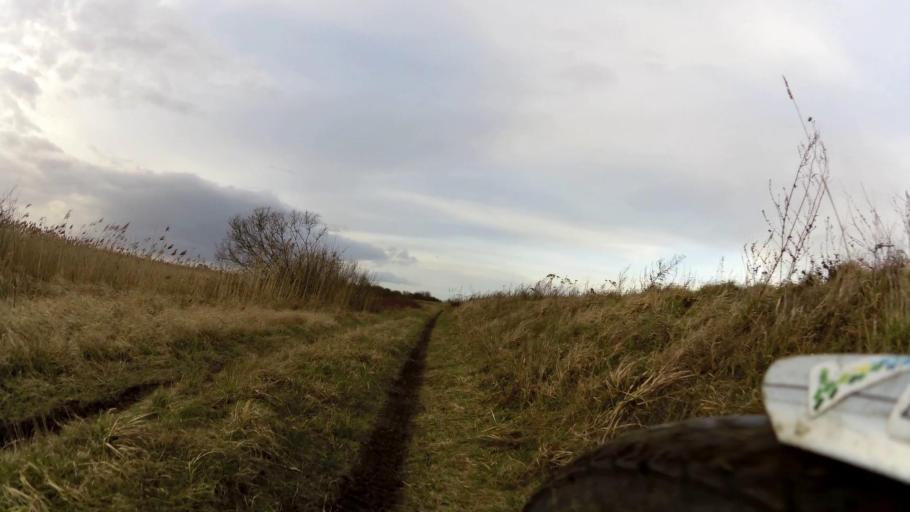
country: PL
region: West Pomeranian Voivodeship
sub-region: Powiat kamienski
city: Kamien Pomorski
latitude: 53.9299
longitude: 14.7627
